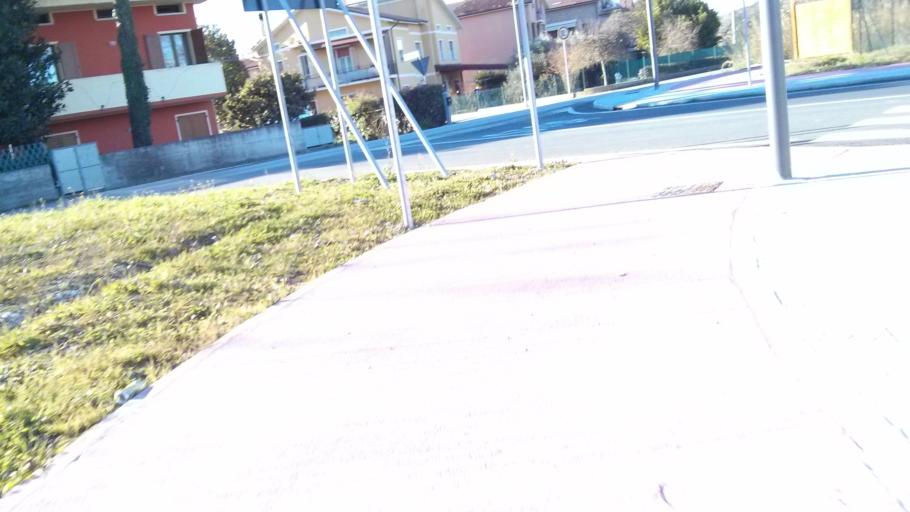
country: IT
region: The Marches
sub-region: Provincia di Pesaro e Urbino
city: Centinarola
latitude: 43.8390
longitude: 12.9997
